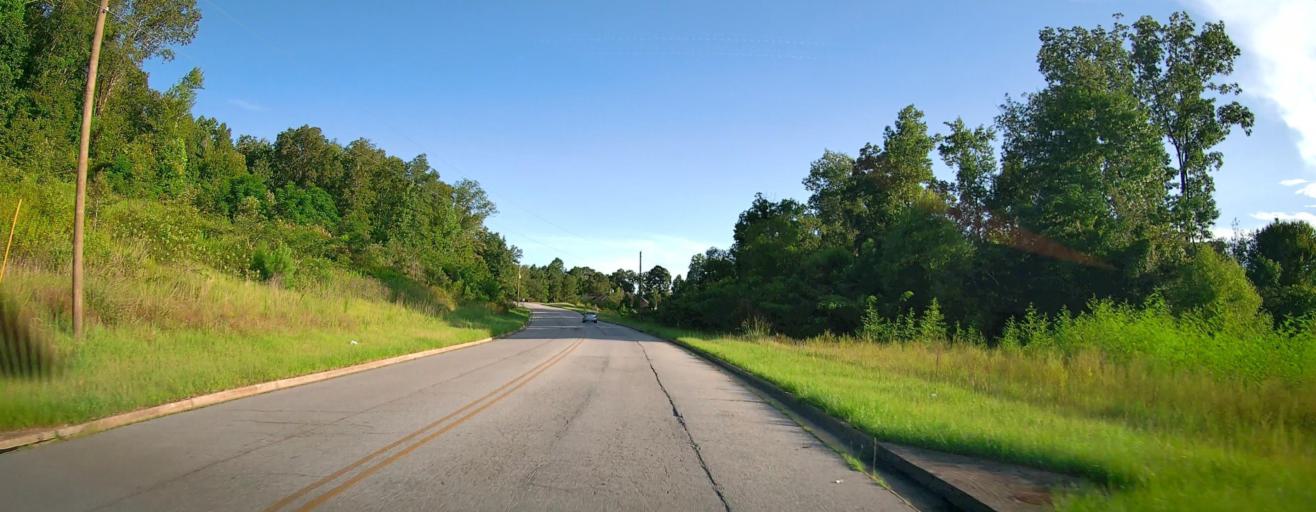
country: US
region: Alabama
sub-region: Russell County
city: Phenix City
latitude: 32.4252
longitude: -85.0349
